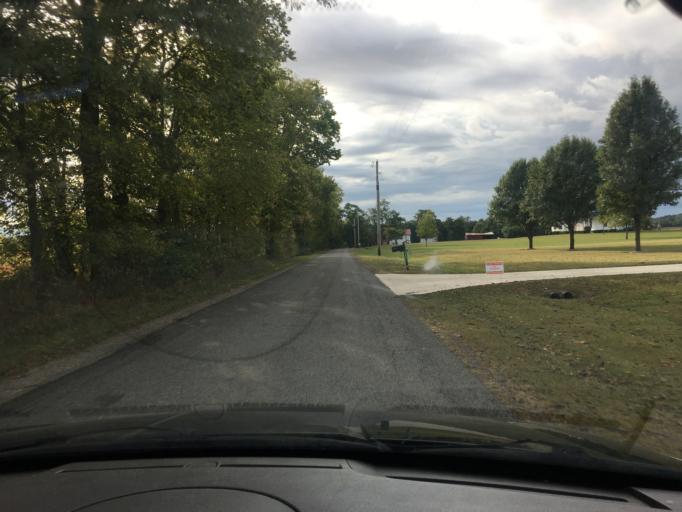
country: US
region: Ohio
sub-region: Logan County
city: West Liberty
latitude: 40.2569
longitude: -83.7338
